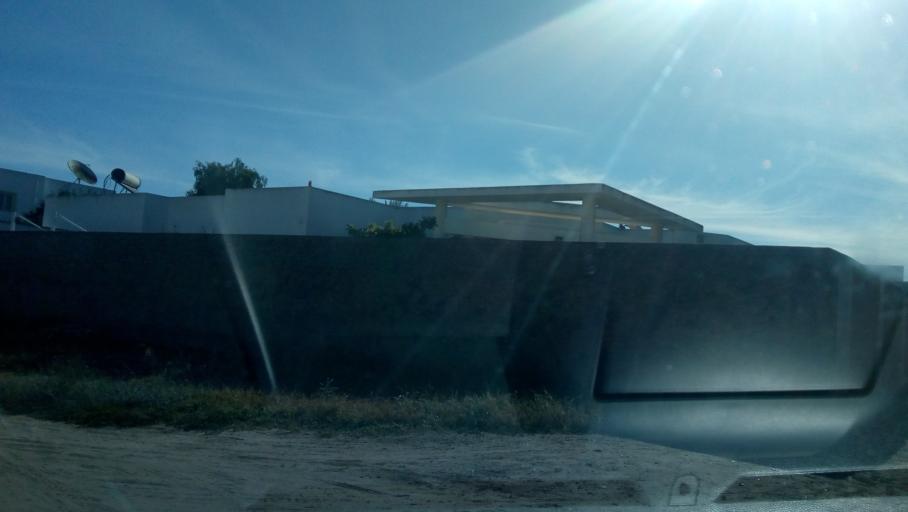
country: TN
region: Safaqis
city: Sfax
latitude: 34.7512
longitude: 10.7335
